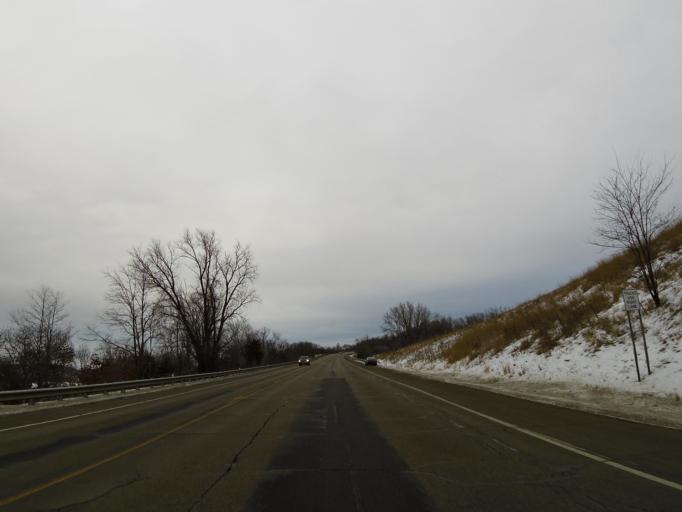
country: US
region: Wisconsin
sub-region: Saint Croix County
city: North Hudson
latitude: 44.9961
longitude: -92.7779
